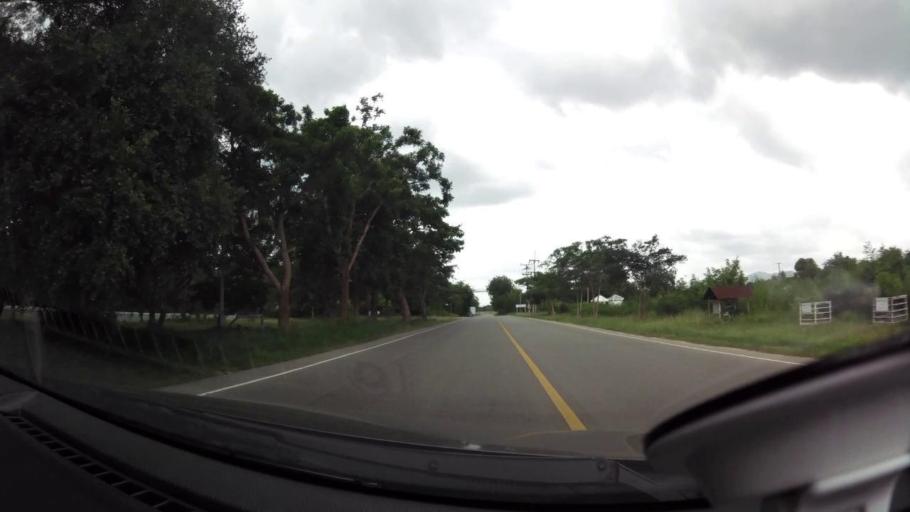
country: TH
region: Phetchaburi
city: Cha-am
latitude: 12.7013
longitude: 99.9584
